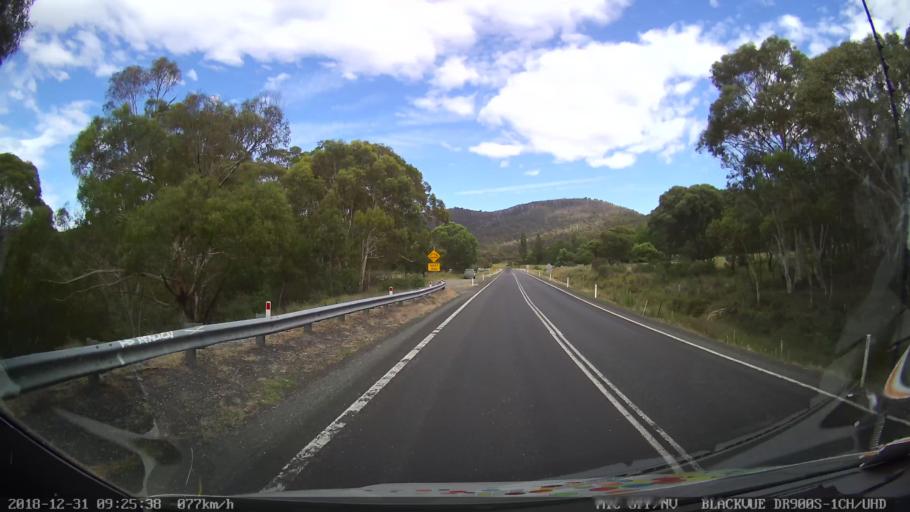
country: AU
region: New South Wales
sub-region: Snowy River
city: Jindabyne
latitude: -36.4441
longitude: 148.5048
